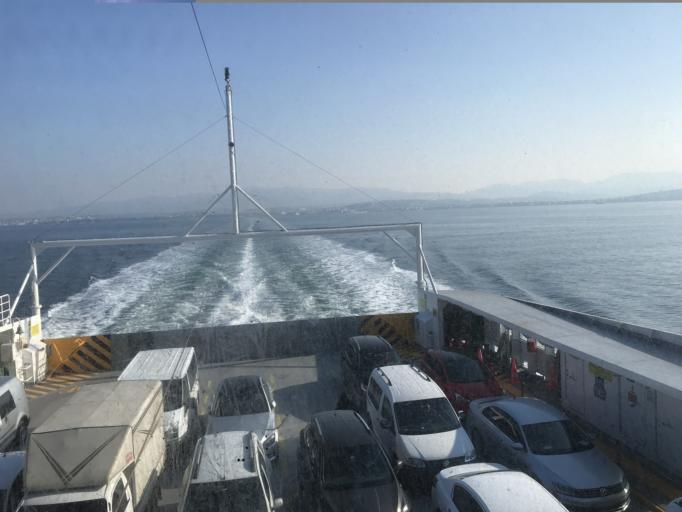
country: TR
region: Yalova
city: Yalova
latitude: 40.6894
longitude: 29.2569
